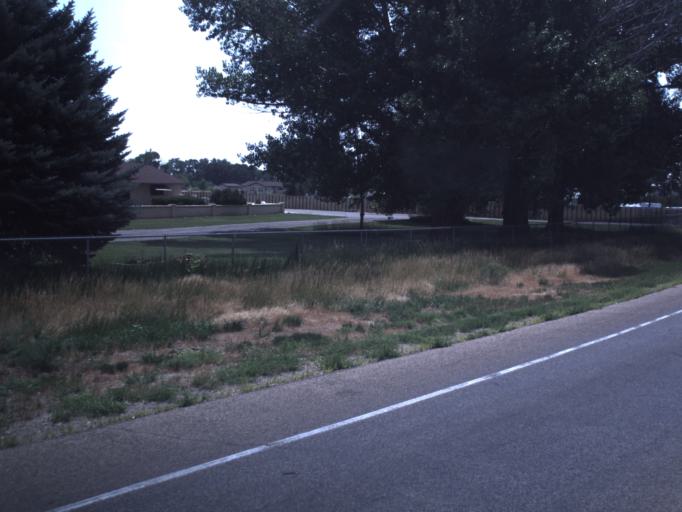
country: US
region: Utah
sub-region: Uintah County
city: Vernal
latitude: 40.5041
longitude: -109.5292
